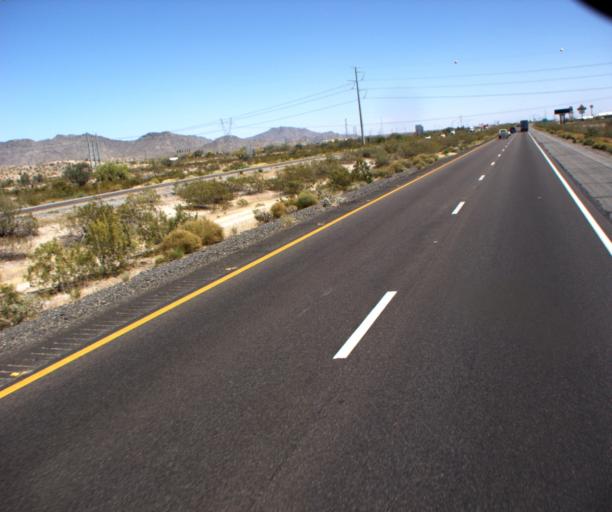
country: US
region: Arizona
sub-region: Maricopa County
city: Buckeye
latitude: 33.4296
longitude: -112.6027
